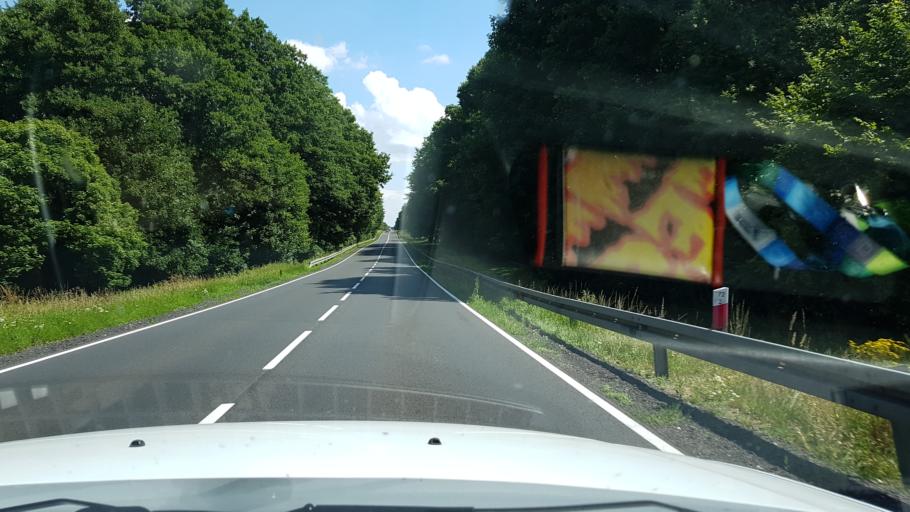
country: PL
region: West Pomeranian Voivodeship
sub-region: Powiat stargardzki
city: Suchan
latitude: 53.2755
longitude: 15.3909
